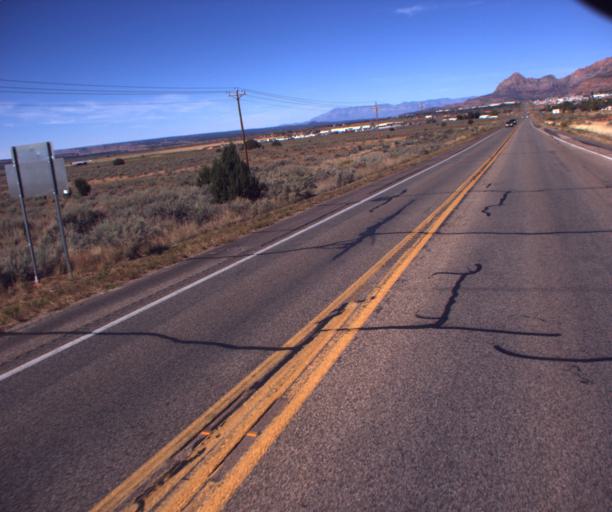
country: US
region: Arizona
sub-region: Mohave County
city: Colorado City
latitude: 36.9726
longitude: -112.9766
